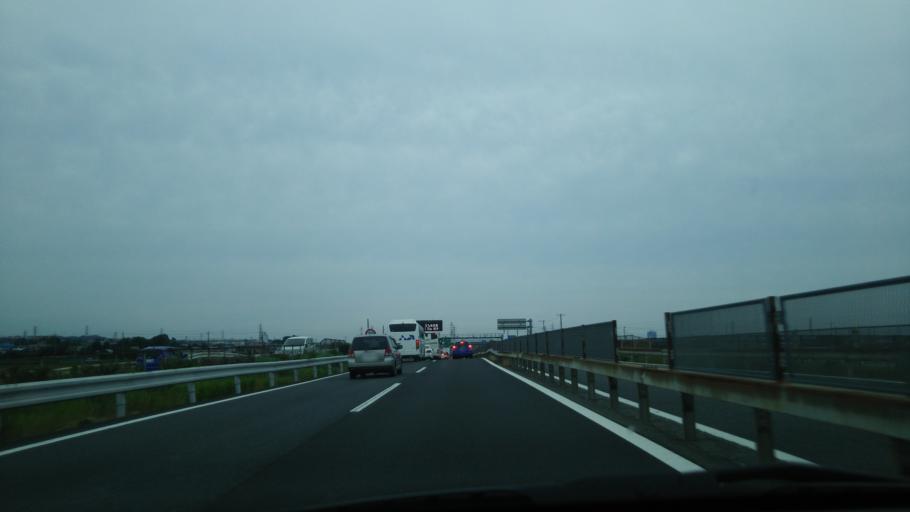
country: JP
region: Kanagawa
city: Isehara
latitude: 35.3810
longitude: 139.3293
